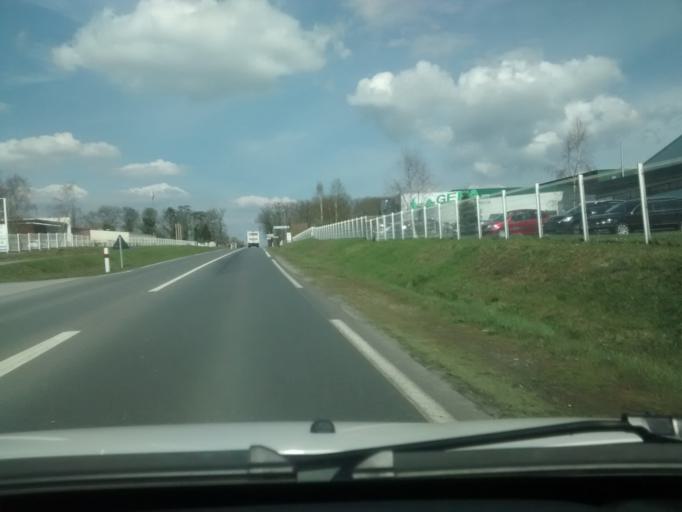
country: FR
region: Brittany
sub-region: Departement d'Ille-et-Vilaine
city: Chateaugiron
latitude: 48.0589
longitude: -1.5098
